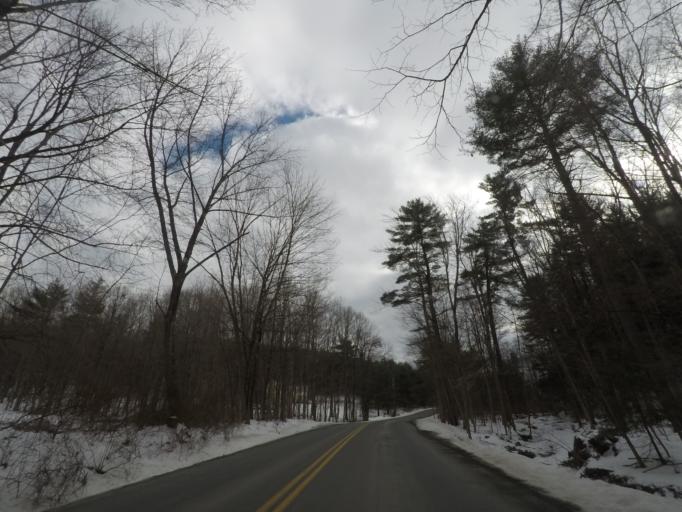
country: US
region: New York
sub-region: Rensselaer County
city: Hoosick Falls
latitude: 42.8907
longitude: -73.4200
